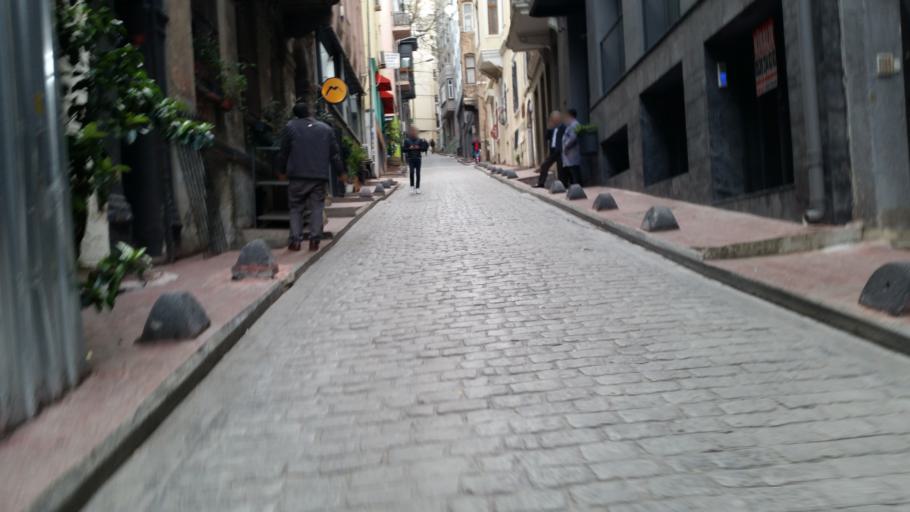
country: TR
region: Istanbul
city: Eminoenue
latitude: 41.0265
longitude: 28.9766
